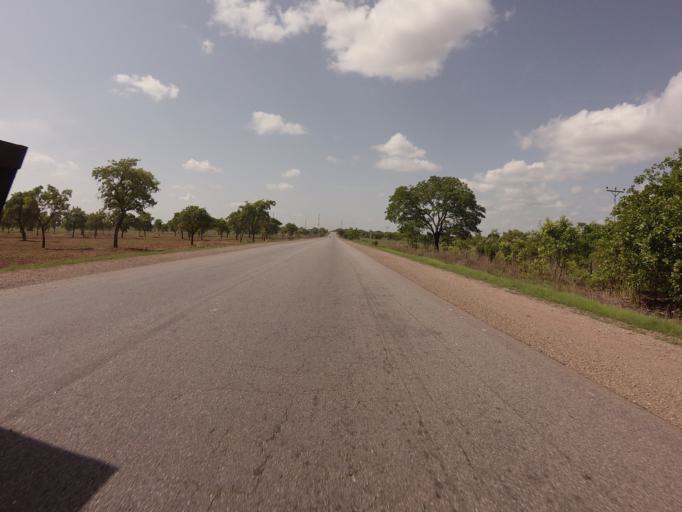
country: GH
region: Northern
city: Savelugu
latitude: 9.9704
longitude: -0.8289
